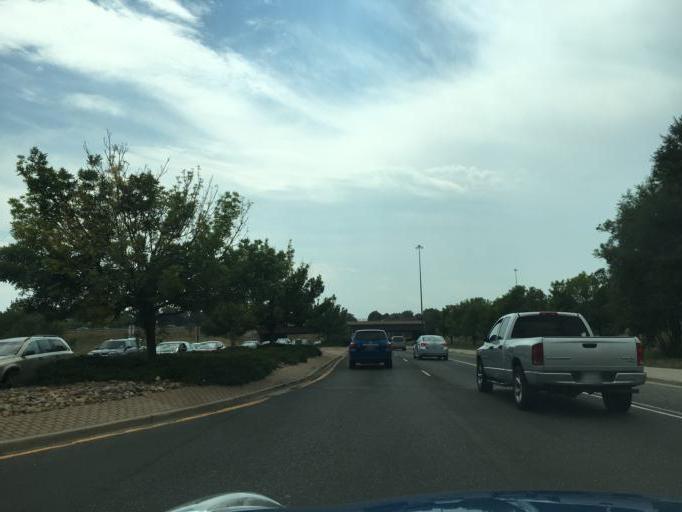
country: US
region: Colorado
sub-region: Jefferson County
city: Arvada
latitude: 39.7883
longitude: -105.0815
